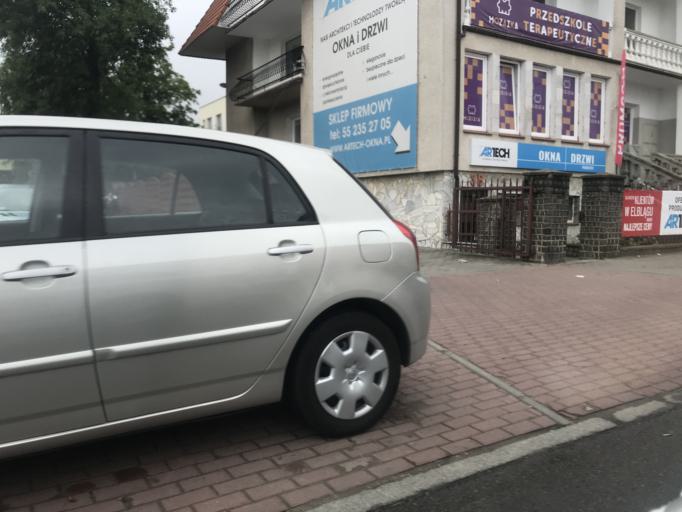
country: PL
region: Warmian-Masurian Voivodeship
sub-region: Powiat elblaski
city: Elblag
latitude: 54.1534
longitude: 19.4191
